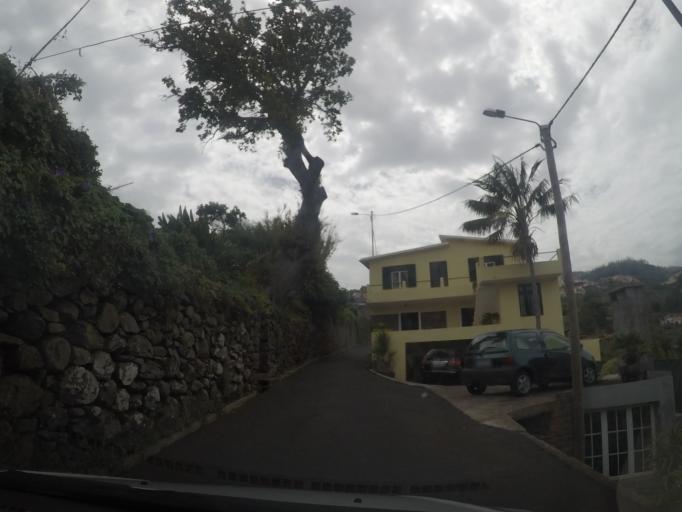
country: PT
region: Madeira
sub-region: Santa Cruz
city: Santa Cruz
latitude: 32.6865
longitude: -16.8069
